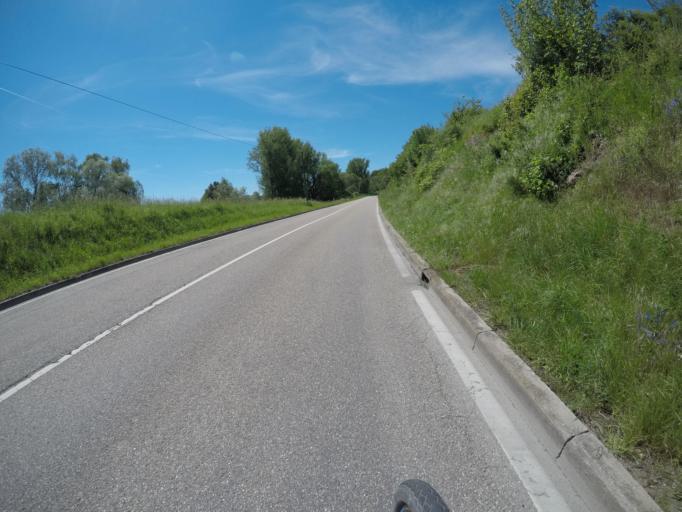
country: DE
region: Baden-Wuerttemberg
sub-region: Karlsruhe Region
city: Heimsheim
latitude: 48.7961
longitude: 8.8348
